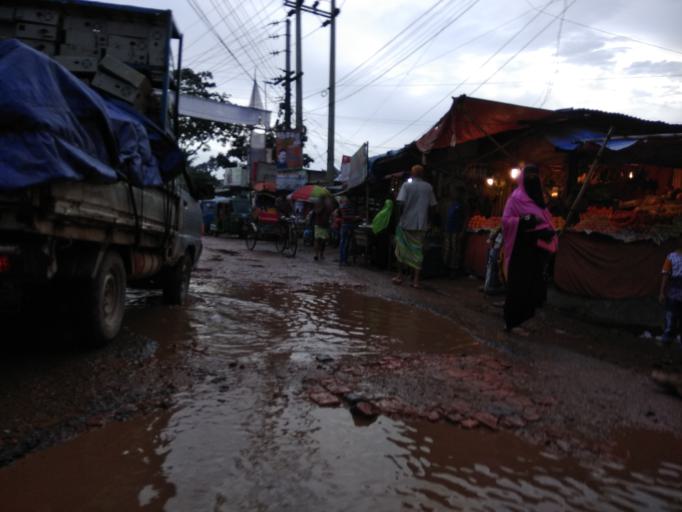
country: BD
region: Dhaka
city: Azimpur
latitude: 23.6860
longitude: 90.3080
